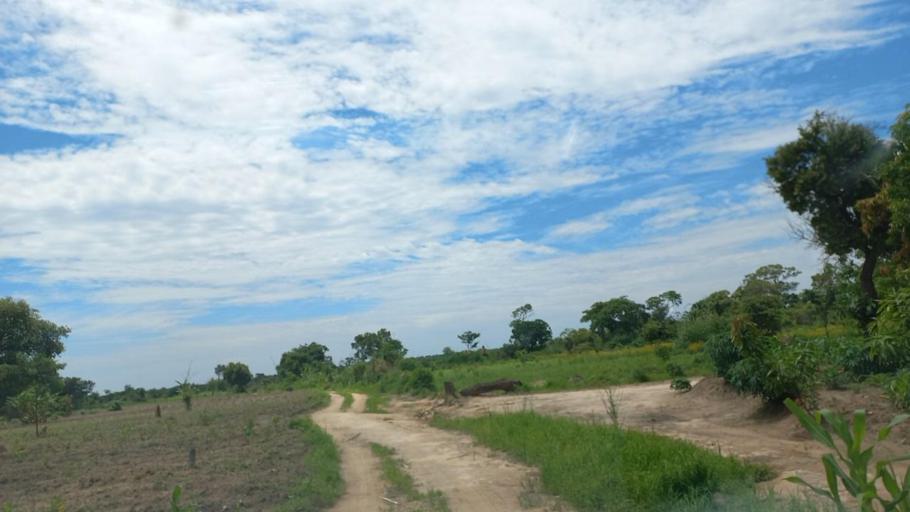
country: ZM
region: Copperbelt
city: Kitwe
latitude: -12.8029
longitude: 28.4011
